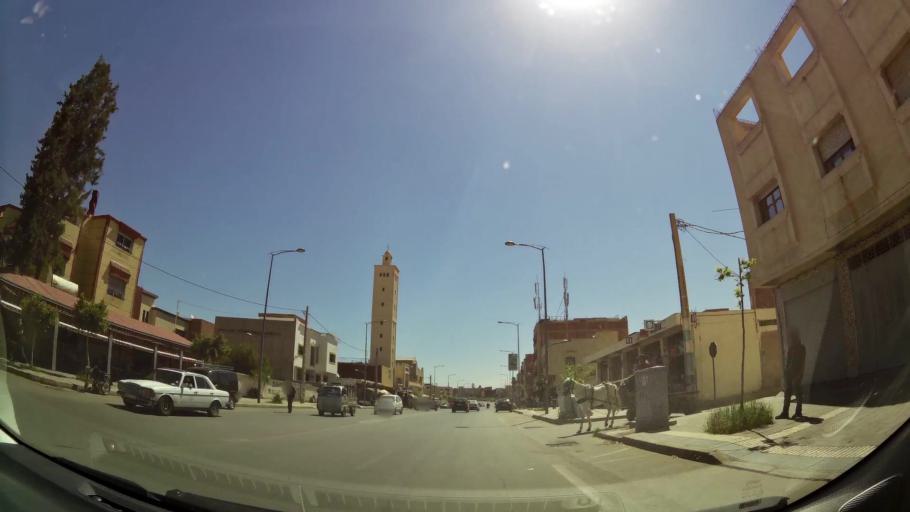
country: MA
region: Oriental
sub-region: Oujda-Angad
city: Oujda
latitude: 34.6656
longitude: -1.8871
